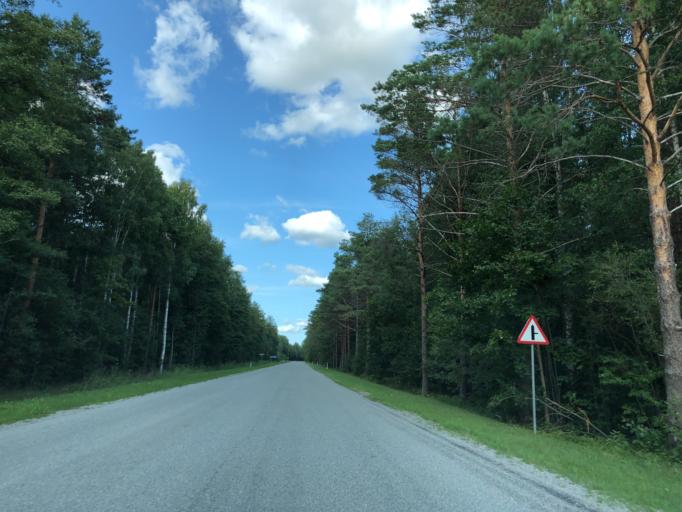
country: EE
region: Hiiumaa
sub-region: Kaerdla linn
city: Kardla
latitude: 58.8148
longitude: 22.7356
